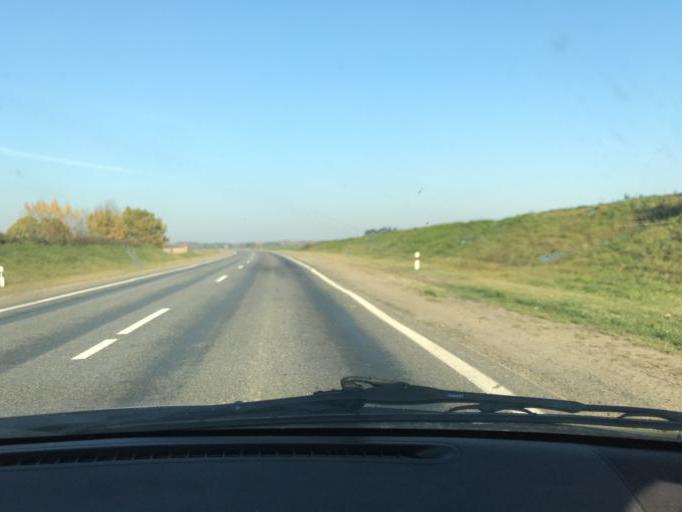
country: BY
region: Vitebsk
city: Orsha
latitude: 54.4169
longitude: 30.4682
